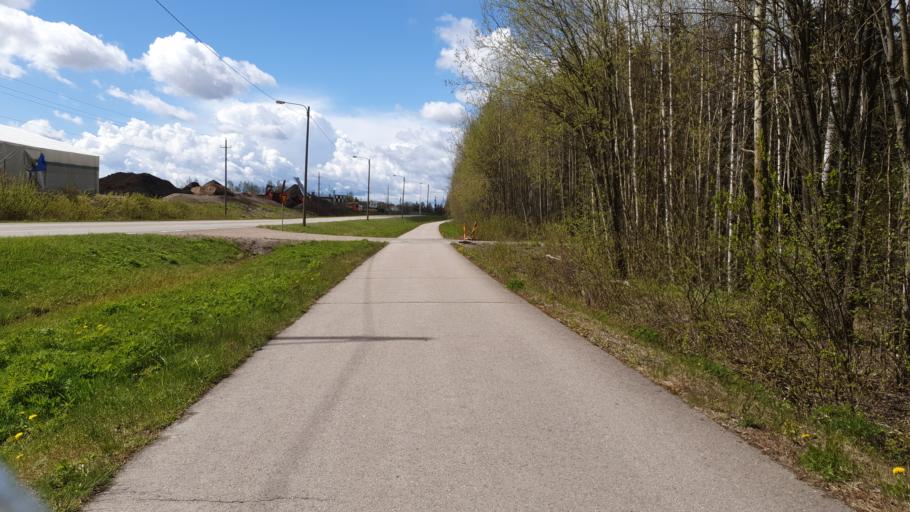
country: FI
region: Uusimaa
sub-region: Helsinki
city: Tuusula
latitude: 60.3383
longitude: 24.9307
